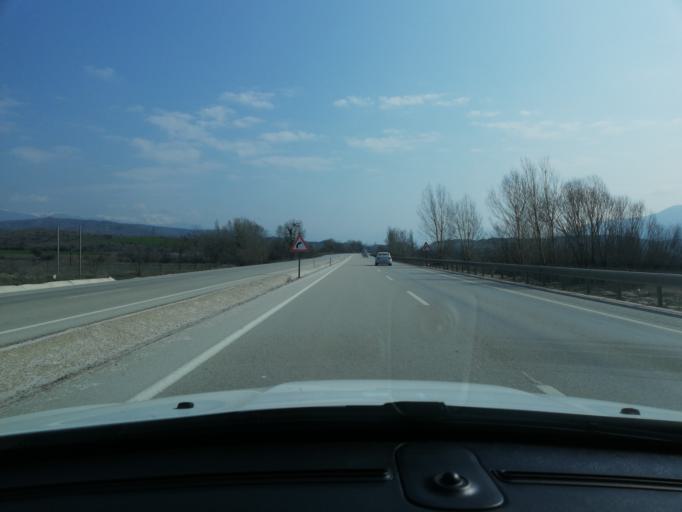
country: TR
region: Cankiri
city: Beloren
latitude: 40.8719
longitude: 33.4967
